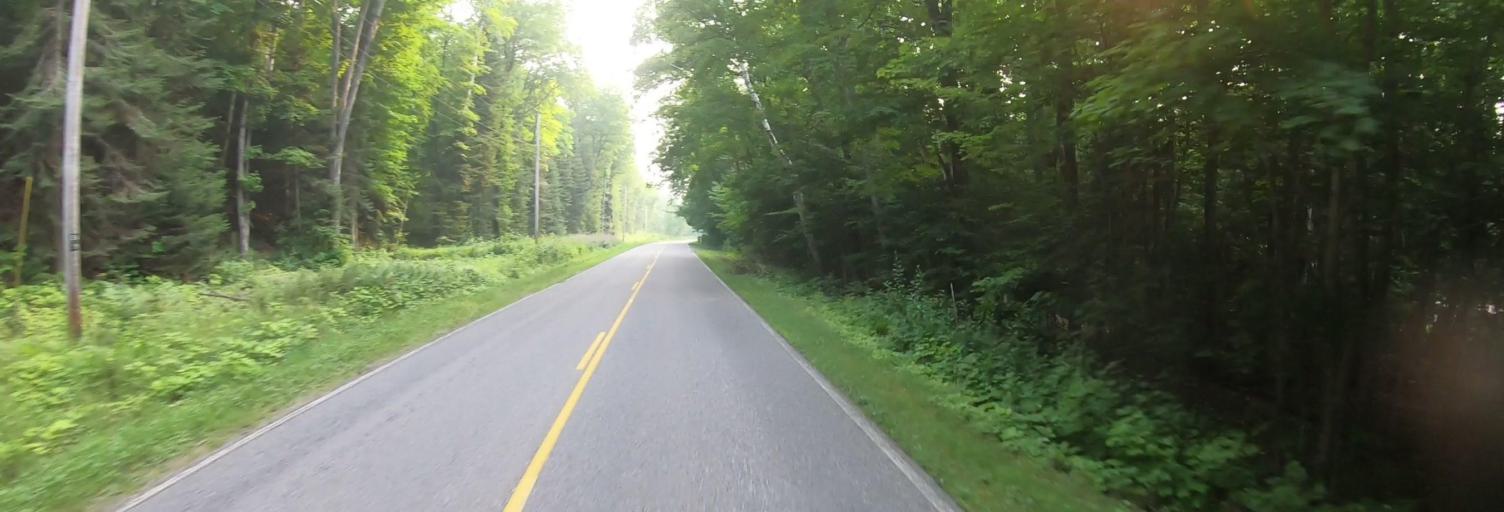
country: US
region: Michigan
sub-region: Chippewa County
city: Sault Ste. Marie
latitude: 46.4660
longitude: -84.7261
